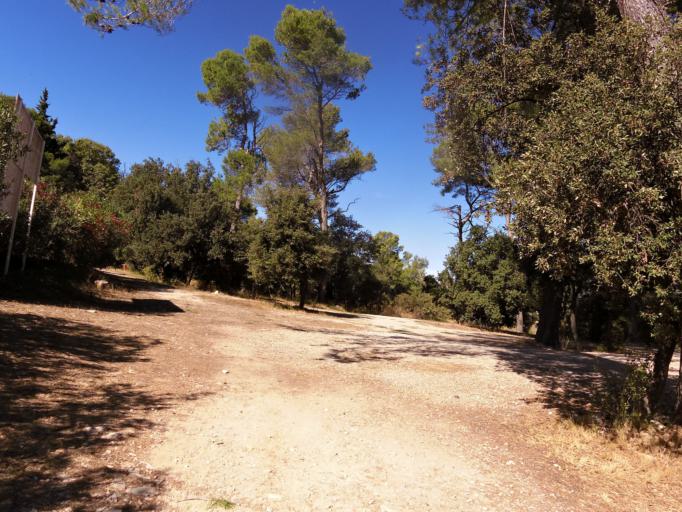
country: FR
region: Languedoc-Roussillon
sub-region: Departement du Gard
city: Nages-et-Solorgues
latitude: 43.7707
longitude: 4.2353
